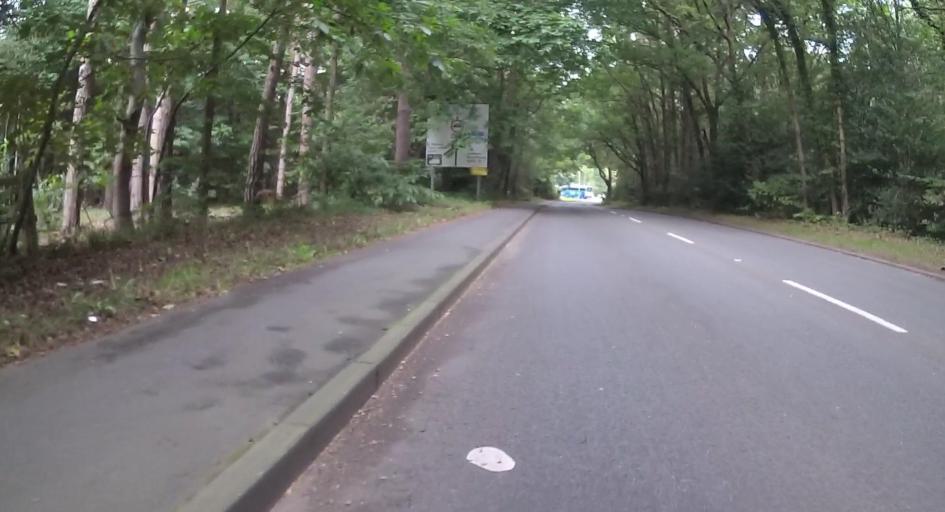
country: GB
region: England
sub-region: Surrey
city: Woking
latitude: 51.3315
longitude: -0.5449
